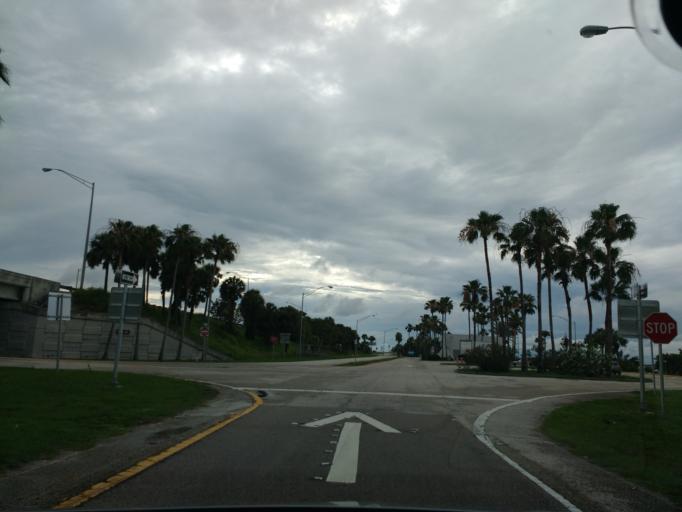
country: US
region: Florida
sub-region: Manatee County
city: Memphis
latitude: 27.5842
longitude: -82.6129
